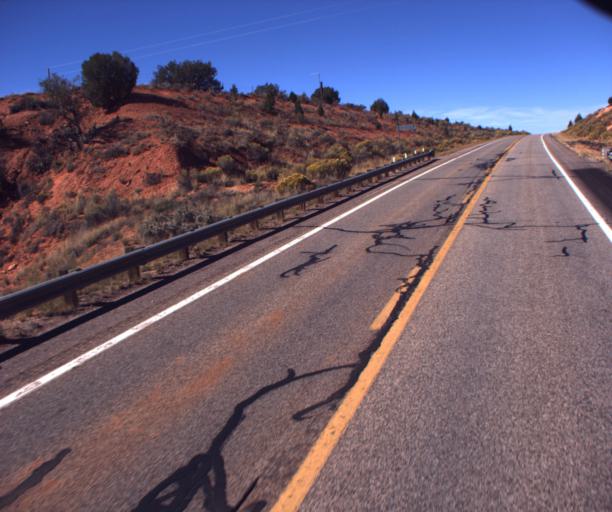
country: US
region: Arizona
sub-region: Mohave County
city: Colorado City
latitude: 36.8812
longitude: -112.8952
